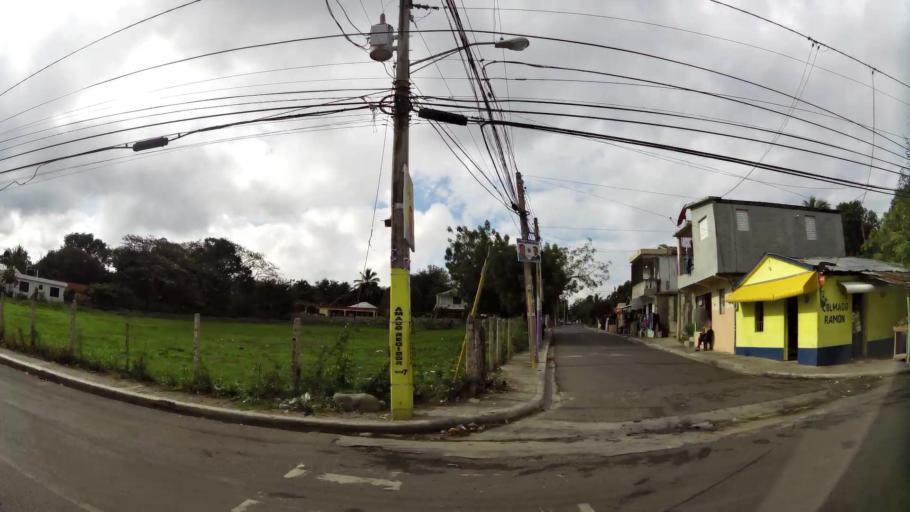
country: DO
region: Santiago
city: Santiago de los Caballeros
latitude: 19.4264
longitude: -70.6581
